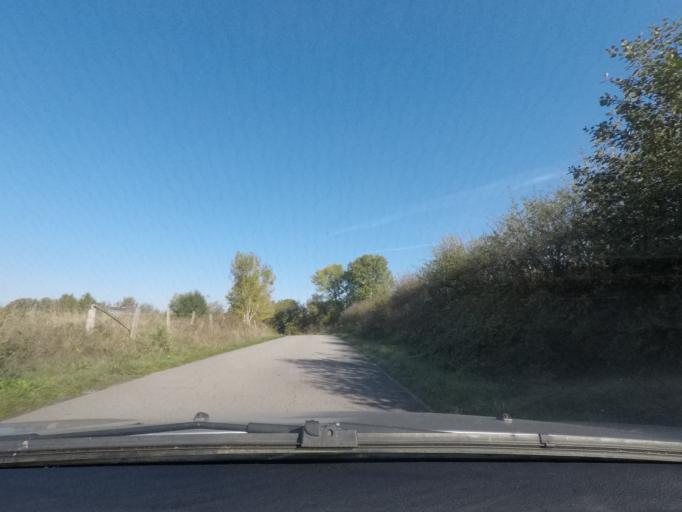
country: BE
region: Wallonia
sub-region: Province du Luxembourg
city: Habay-la-Vieille
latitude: 49.7163
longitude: 5.5662
